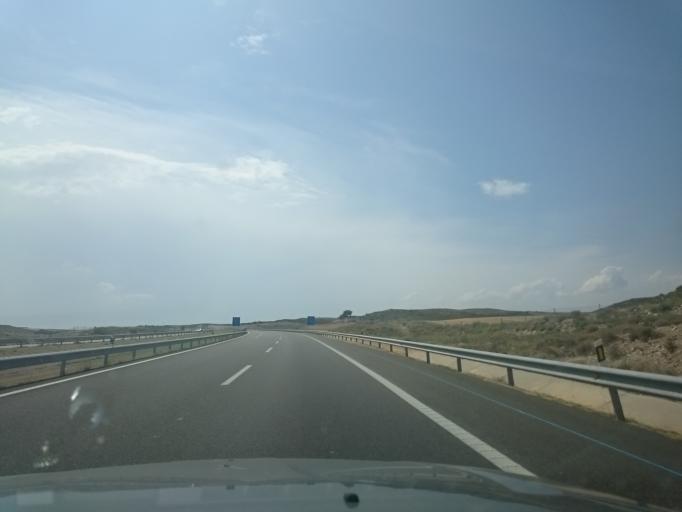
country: ES
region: Aragon
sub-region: Provincia de Huesca
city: Penalba
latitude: 41.5145
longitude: -0.0503
